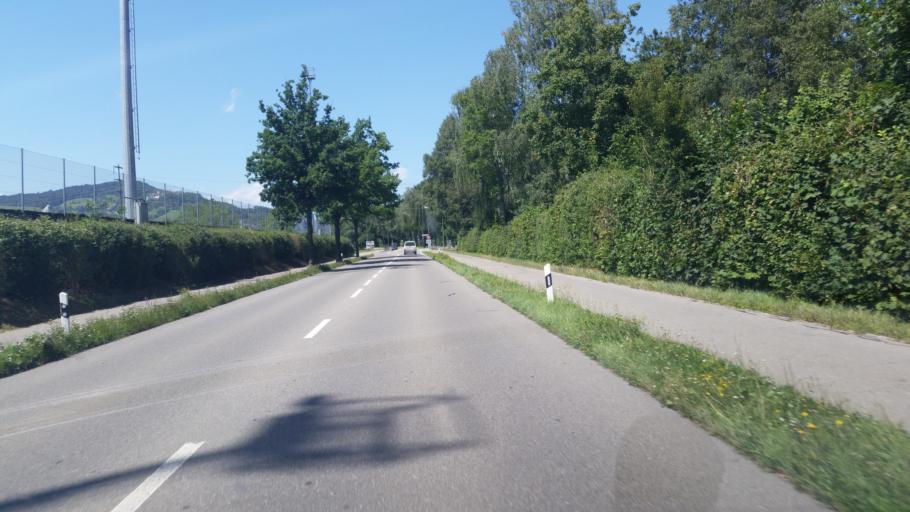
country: CH
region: Zurich
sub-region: Bezirk Dielsdorf
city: Niederhasli
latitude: 47.4828
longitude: 8.4752
